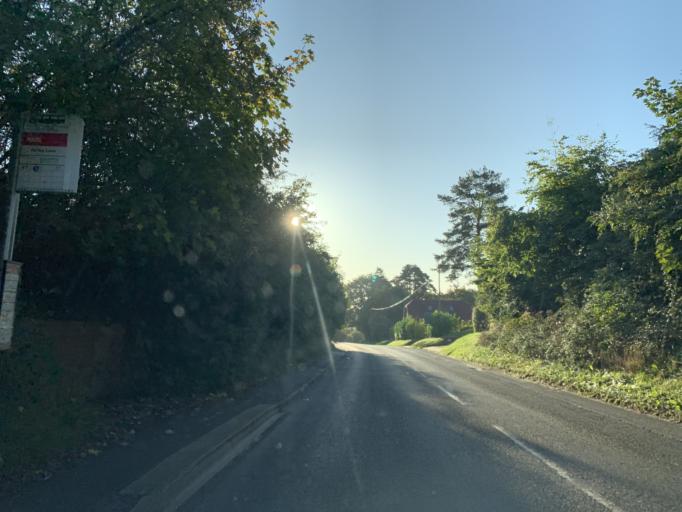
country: GB
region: England
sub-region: Wiltshire
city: Alderbury
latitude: 51.0447
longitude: -1.7362
